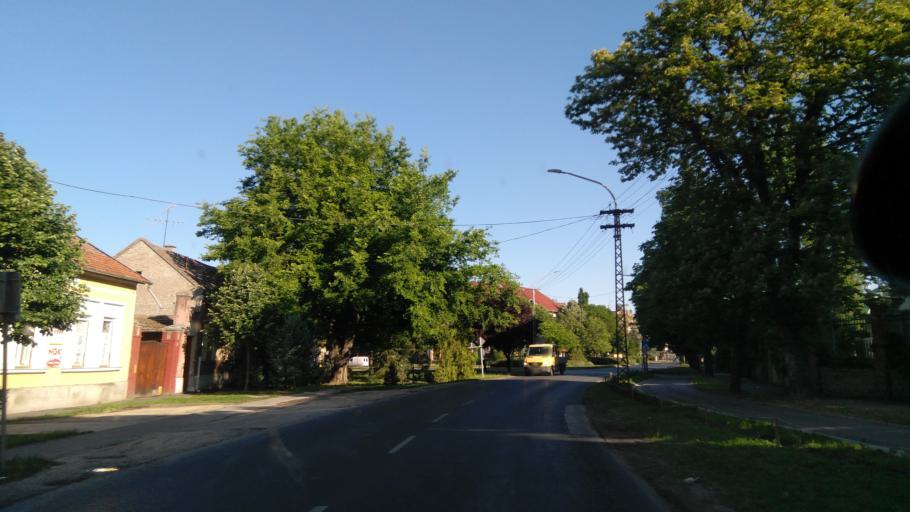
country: HU
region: Bekes
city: Gyula
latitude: 46.6403
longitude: 21.2747
